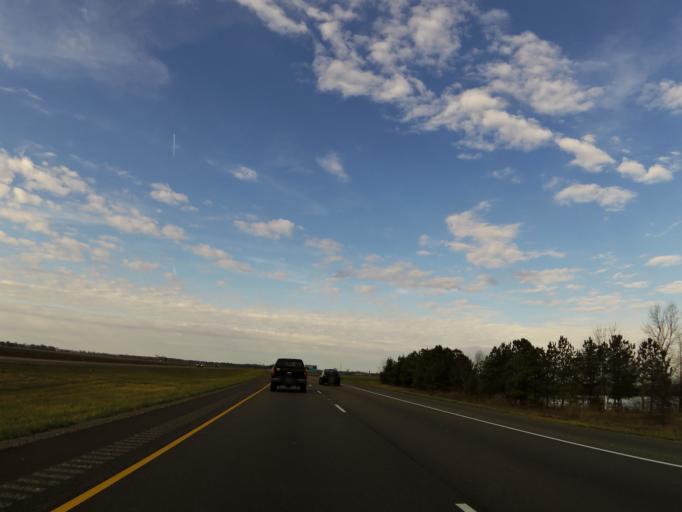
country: US
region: Illinois
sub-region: Washington County
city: Okawville
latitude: 38.4314
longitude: -89.4998
